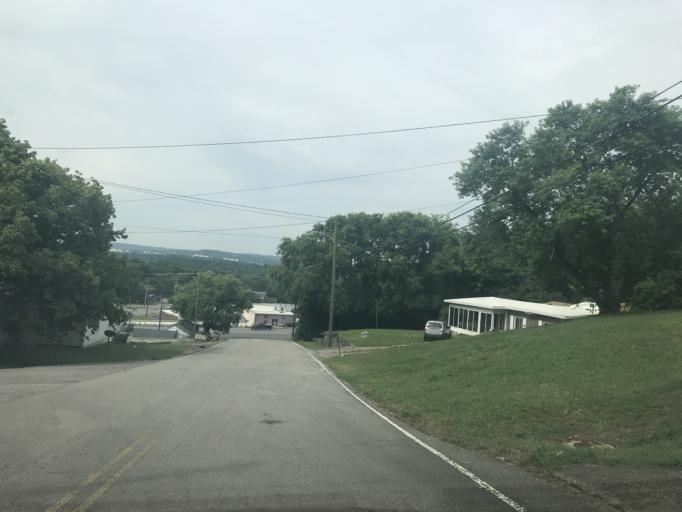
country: US
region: Tennessee
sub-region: Davidson County
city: Nashville
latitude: 36.1960
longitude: -86.8324
